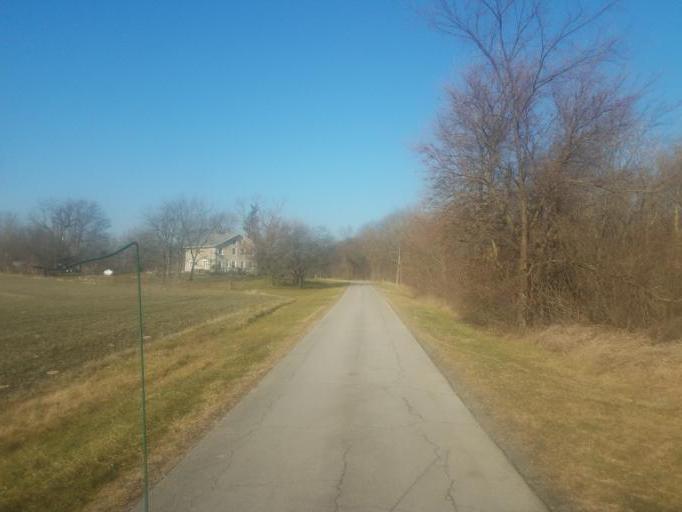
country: US
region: Ohio
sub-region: Seneca County
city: Tiffin
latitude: 41.0614
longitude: -83.0208
